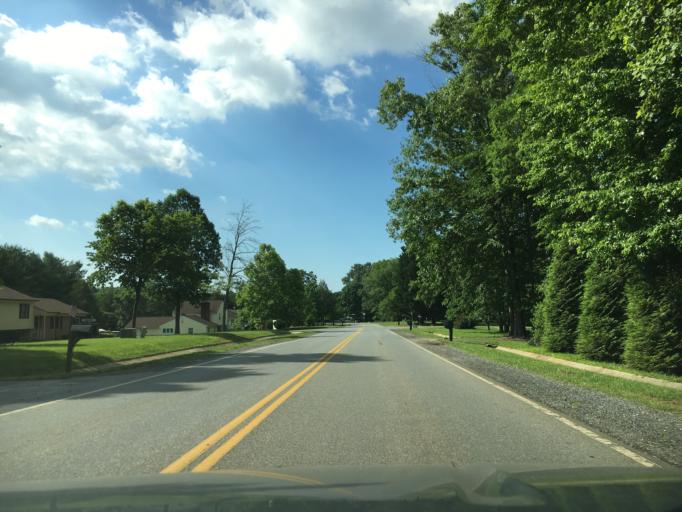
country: US
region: Virginia
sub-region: Bedford County
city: Forest
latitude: 37.3935
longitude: -79.2483
